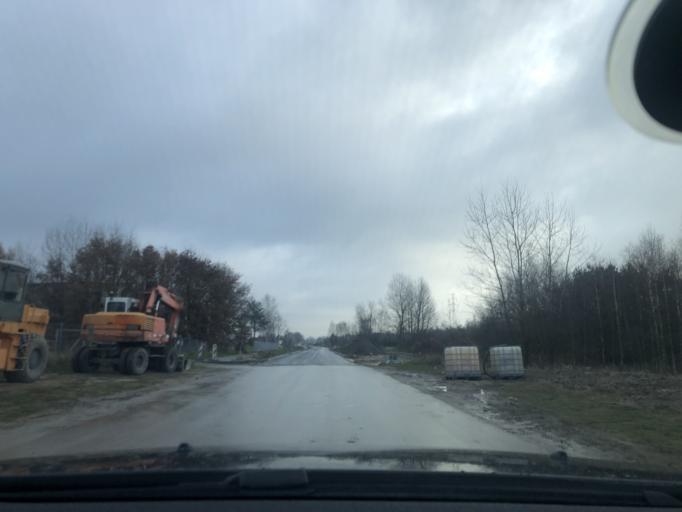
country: PL
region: Swietokrzyskie
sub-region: Powiat jedrzejowski
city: Jedrzejow
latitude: 50.6303
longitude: 20.2827
